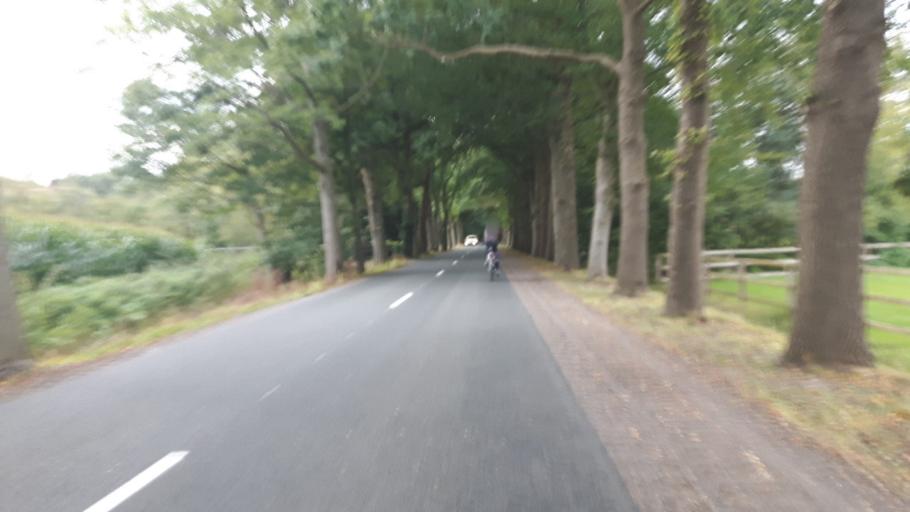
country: NL
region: Gelderland
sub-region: Gemeente Barneveld
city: Zwartebroek
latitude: 52.2067
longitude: 5.5340
